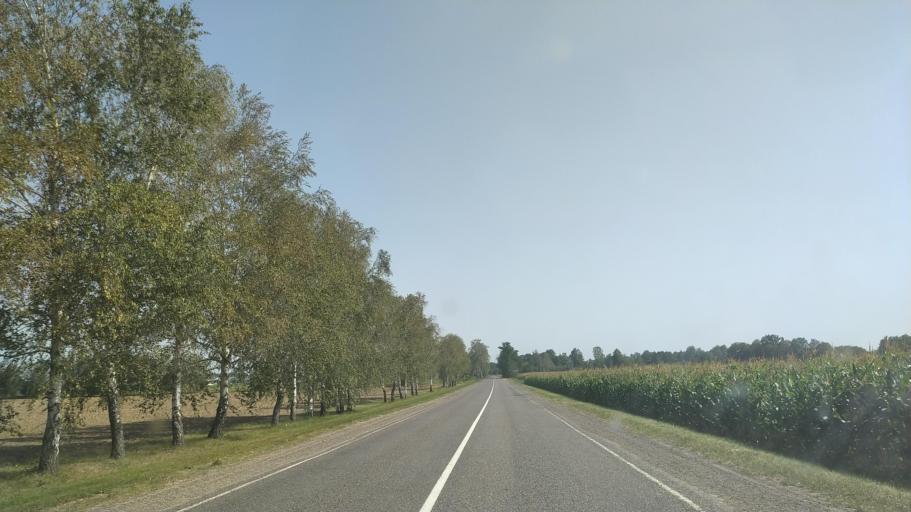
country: BY
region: Brest
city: Byaroza
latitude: 52.3950
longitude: 25.0086
